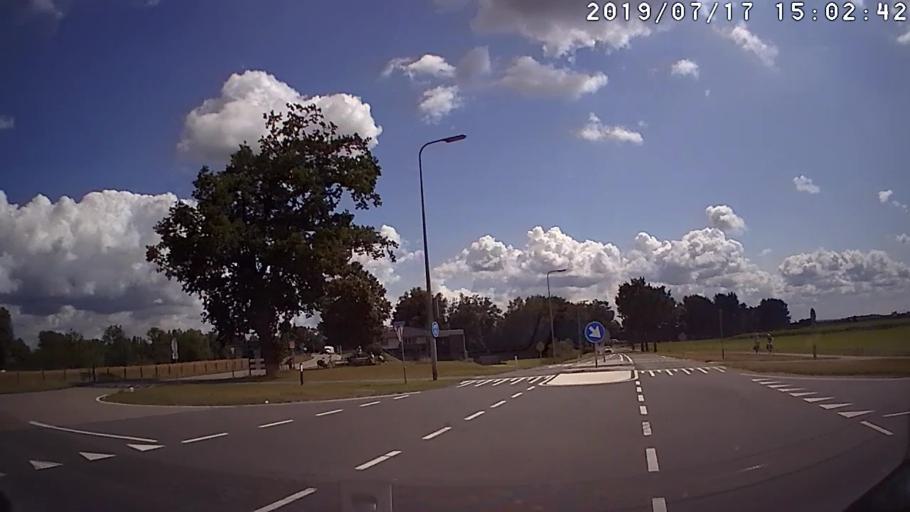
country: NL
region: Overijssel
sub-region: Gemeente Kampen
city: Kampen
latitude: 52.5186
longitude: 5.9561
